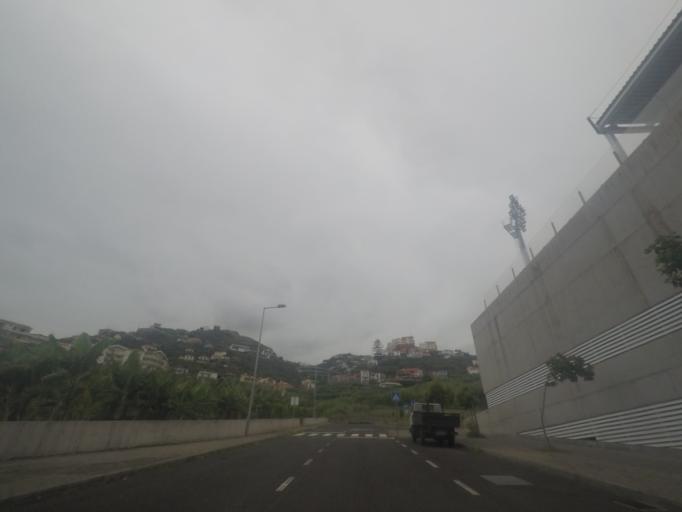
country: PT
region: Madeira
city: Camara de Lobos
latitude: 32.6551
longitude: -16.9831
